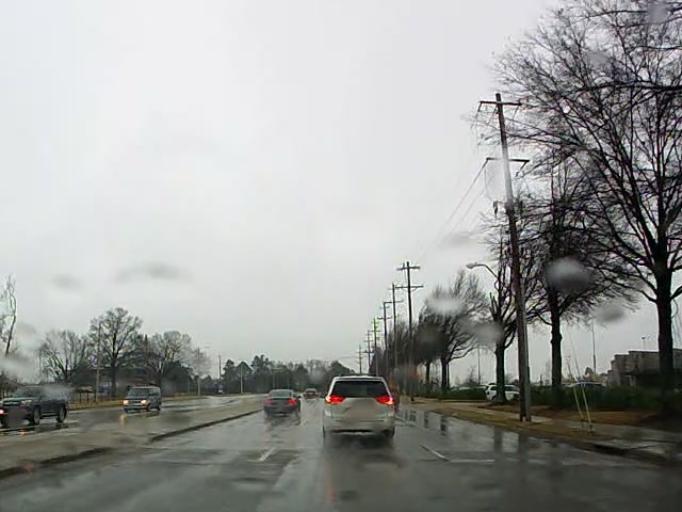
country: US
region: Tennessee
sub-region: Shelby County
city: Germantown
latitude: 35.0993
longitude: -89.8591
